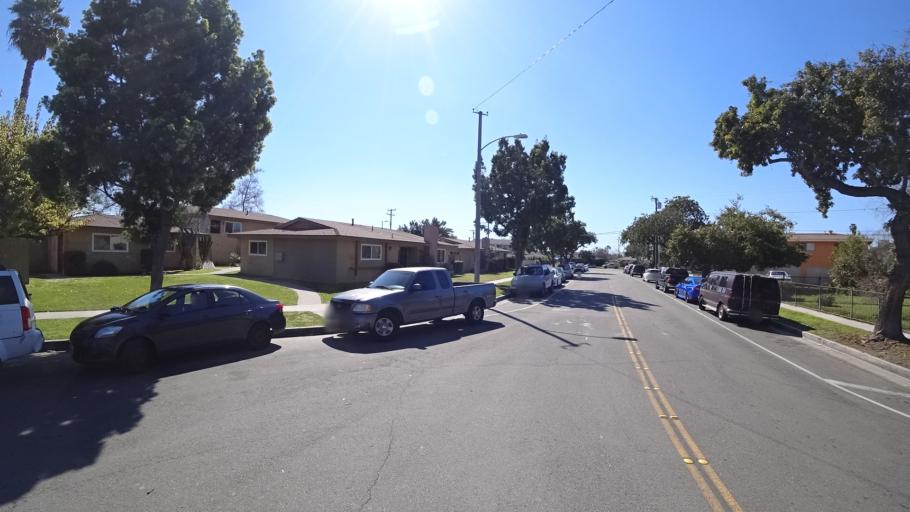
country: US
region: California
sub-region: Orange County
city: Stanton
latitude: 33.8294
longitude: -117.9908
